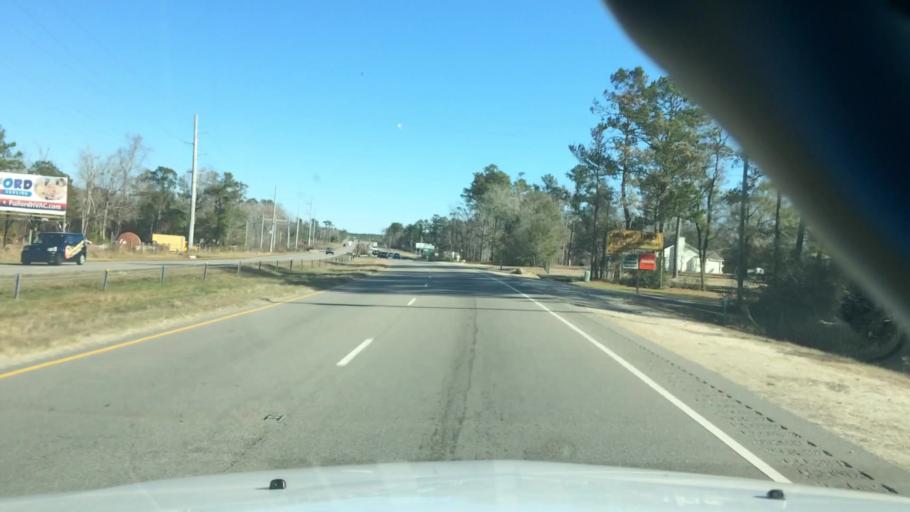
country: US
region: North Carolina
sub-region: Brunswick County
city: Bolivia
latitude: 34.0211
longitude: -78.2650
